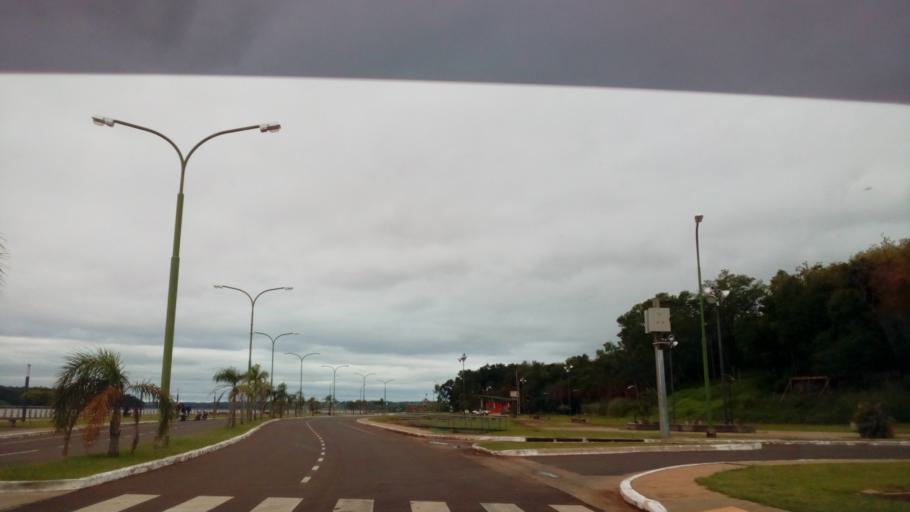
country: AR
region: Misiones
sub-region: Departamento de Candelaria
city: Candelaria
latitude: -27.4492
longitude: -55.7527
